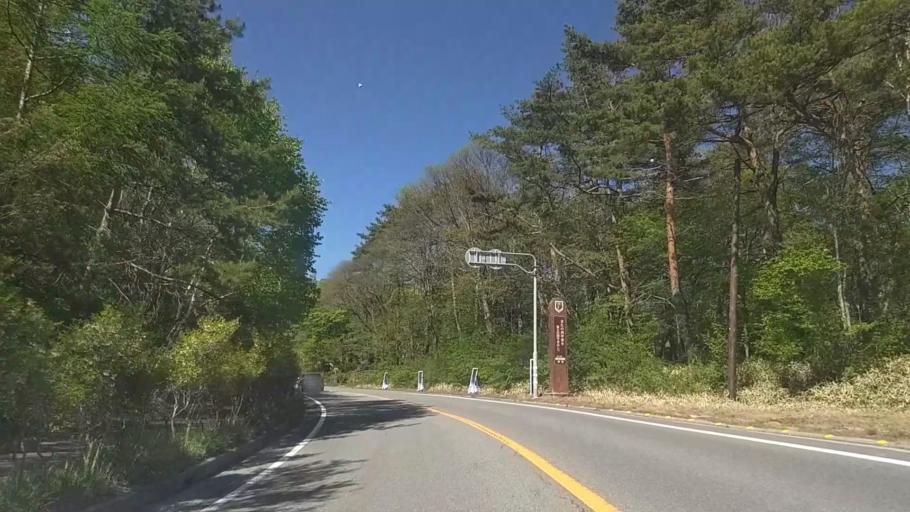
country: JP
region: Yamanashi
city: Nirasaki
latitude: 35.9261
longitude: 138.4407
